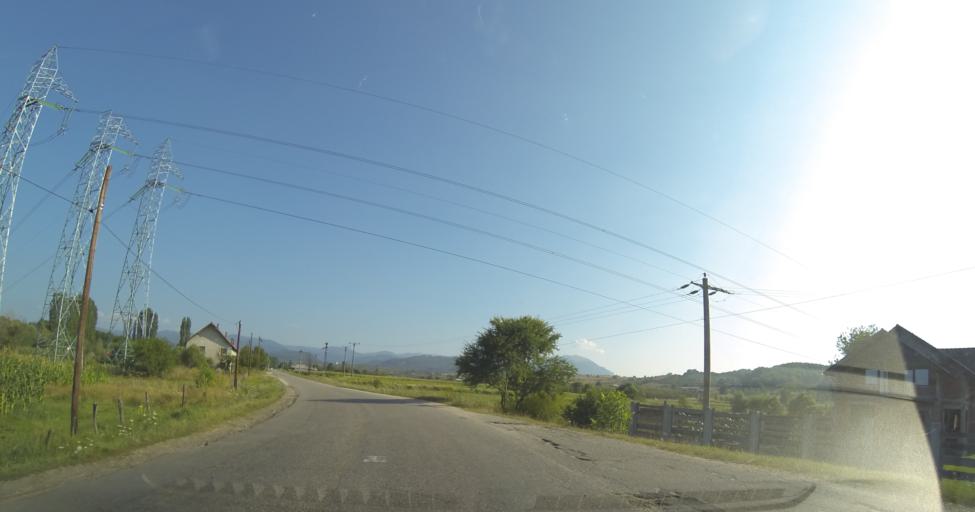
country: RO
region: Valcea
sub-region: Comuna Maldaresti
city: Maldaresti
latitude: 45.1267
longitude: 24.0065
